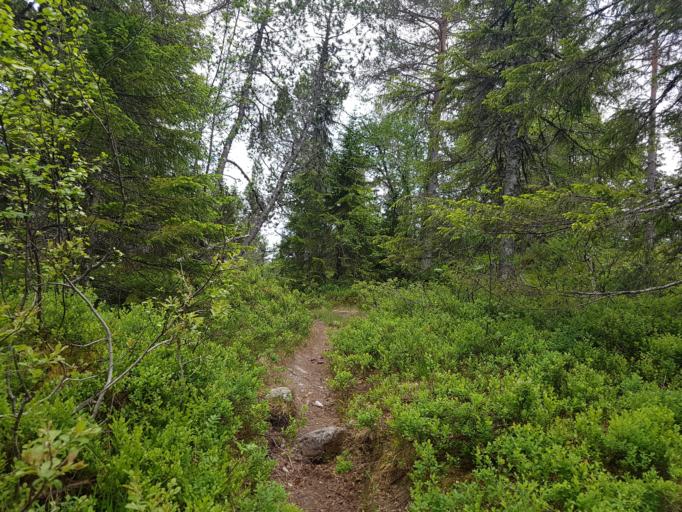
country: NO
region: Sor-Trondelag
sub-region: Trondheim
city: Trondheim
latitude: 63.4100
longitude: 10.3226
